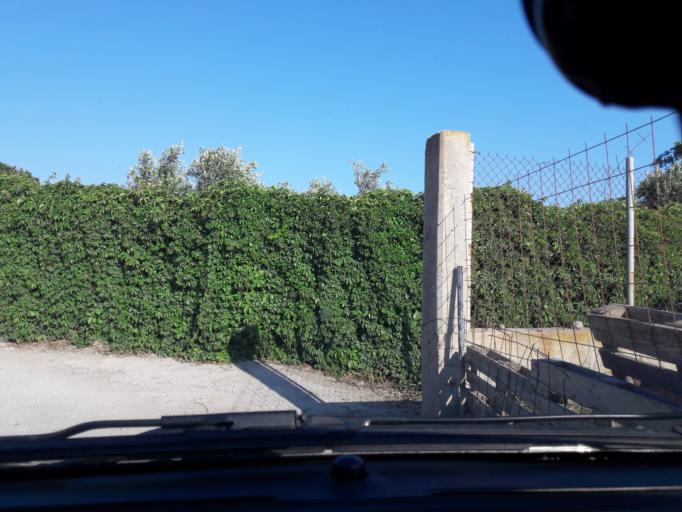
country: GR
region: North Aegean
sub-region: Nomos Lesvou
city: Myrina
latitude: 39.8432
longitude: 25.0804
